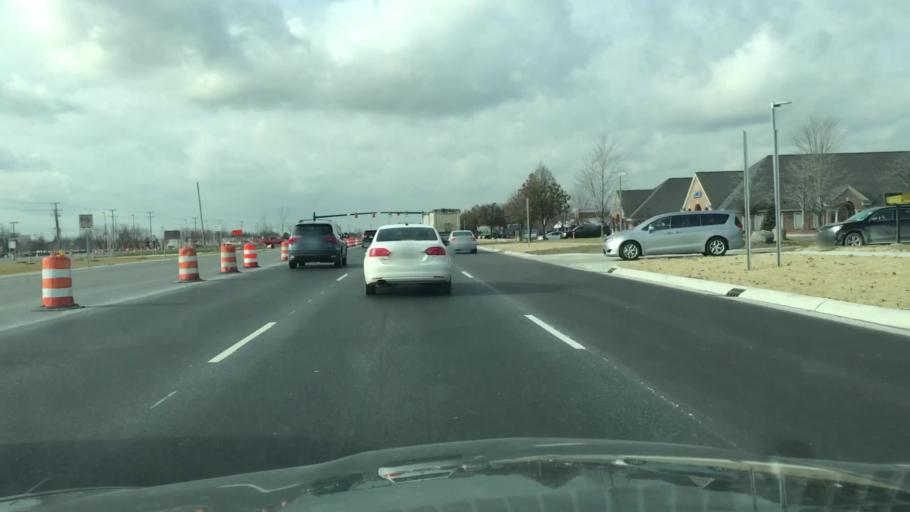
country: US
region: Michigan
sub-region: Macomb County
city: Clinton
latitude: 42.6285
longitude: -82.9415
